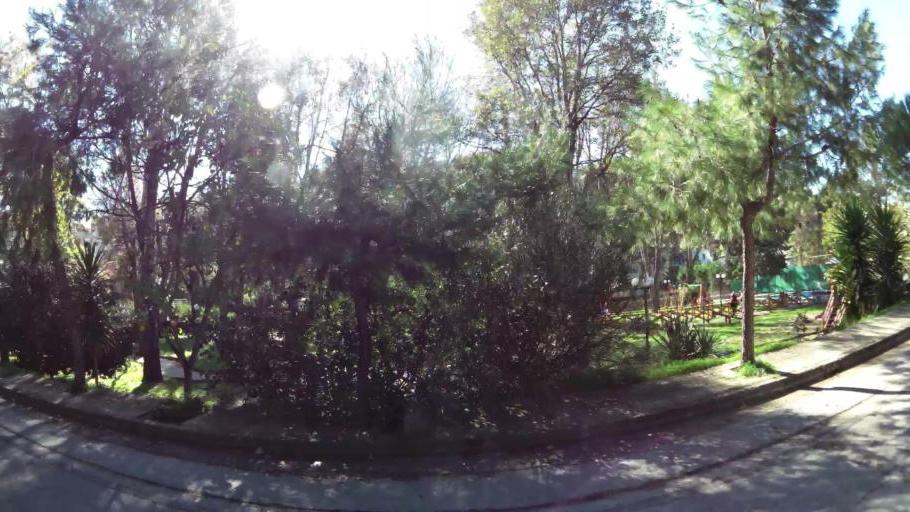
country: GR
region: Attica
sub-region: Nomarchia Anatolikis Attikis
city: Anoixi
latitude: 38.1284
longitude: 23.8592
